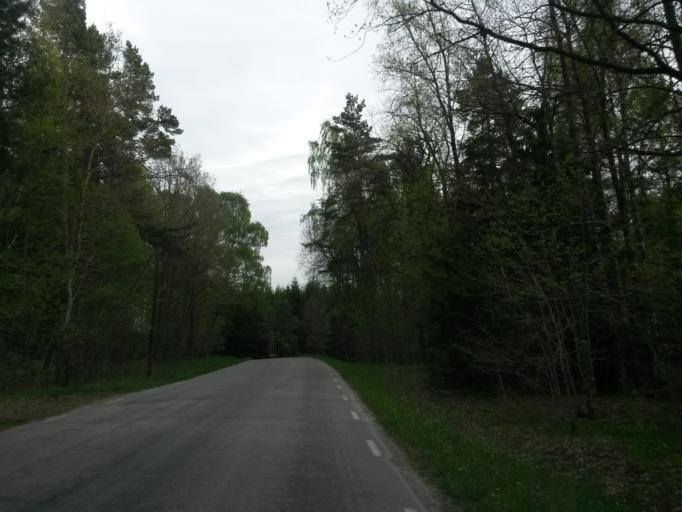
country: SE
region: Vaestra Goetaland
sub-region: Vara Kommun
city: Vara
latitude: 58.3544
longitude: 12.8718
